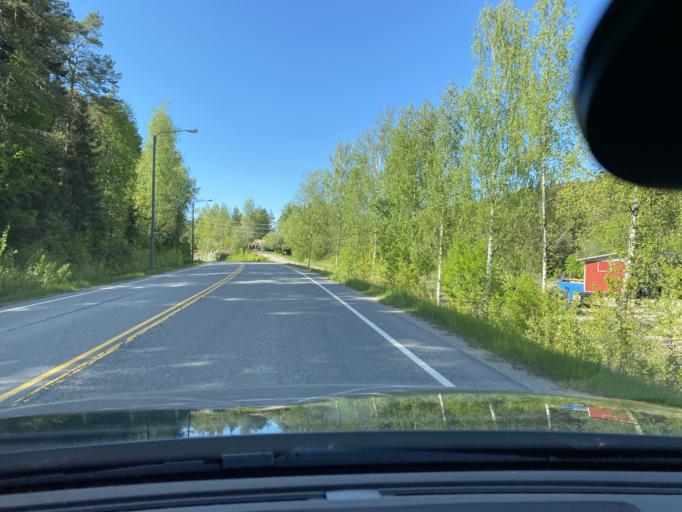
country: FI
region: Varsinais-Suomi
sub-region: Turku
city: Sauvo
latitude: 60.3477
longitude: 22.6820
